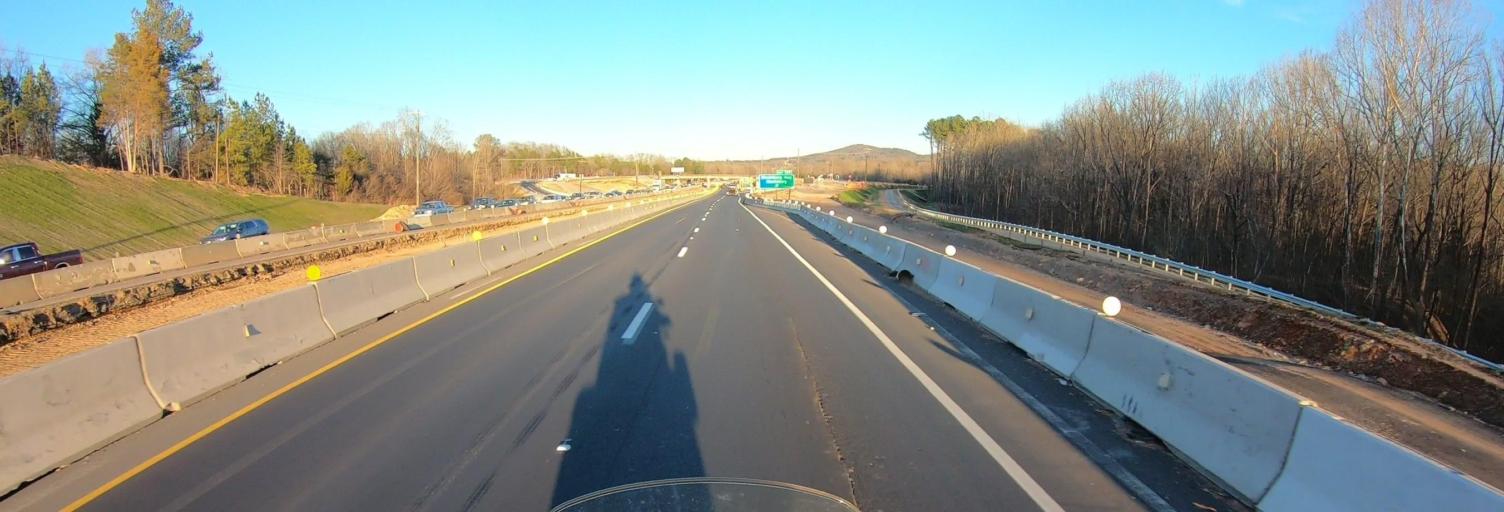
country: US
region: South Carolina
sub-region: Cherokee County
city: Blacksburg
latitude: 35.1270
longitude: -81.5562
